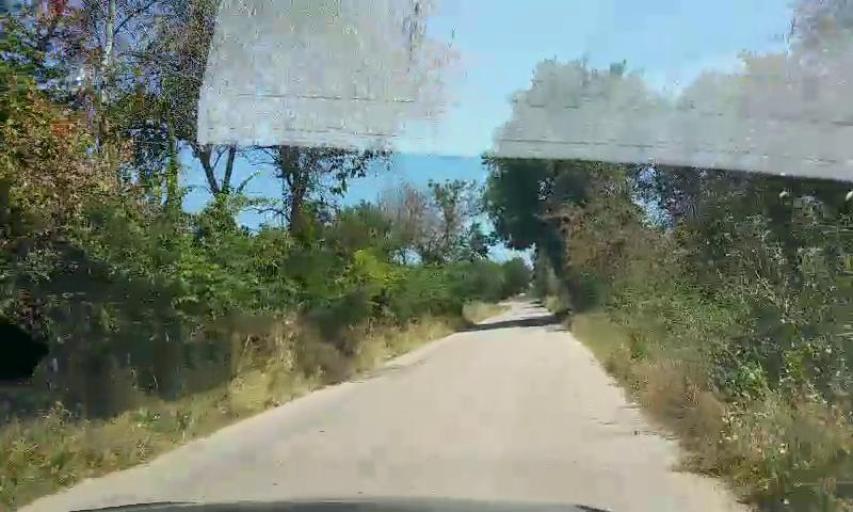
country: IT
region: Molise
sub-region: Provincia di Campobasso
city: Guglionesi
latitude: 41.9526
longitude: 14.9010
